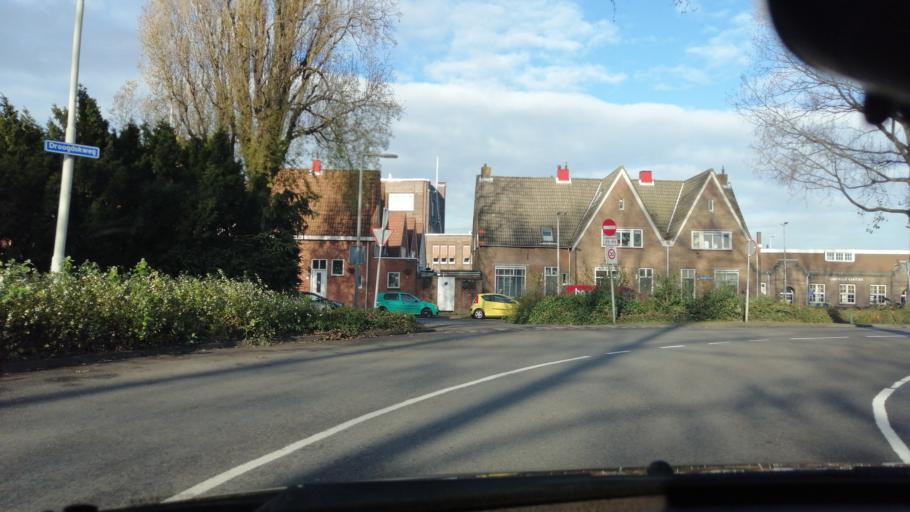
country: NL
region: South Holland
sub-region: Gemeente Rotterdam
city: Delfshaven
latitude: 51.8960
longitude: 4.4219
